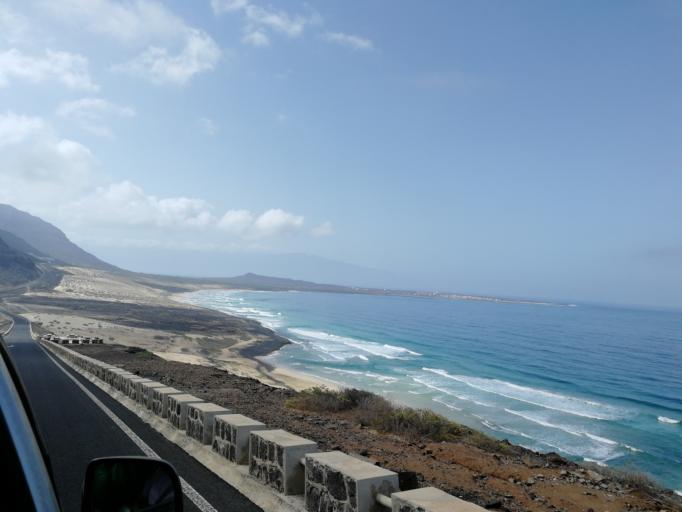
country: CV
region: Sao Vicente
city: Mindelo
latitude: 16.8697
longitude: -24.9025
